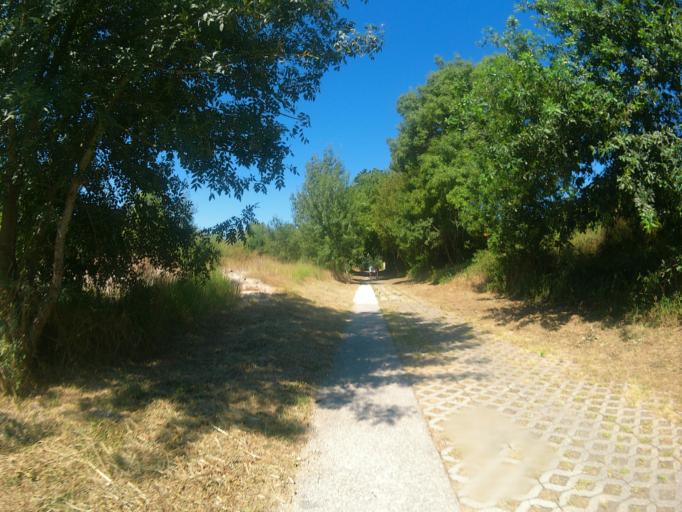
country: PT
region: Viana do Castelo
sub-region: Ponte de Lima
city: Ponte de Lima
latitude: 41.7631
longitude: -8.5962
